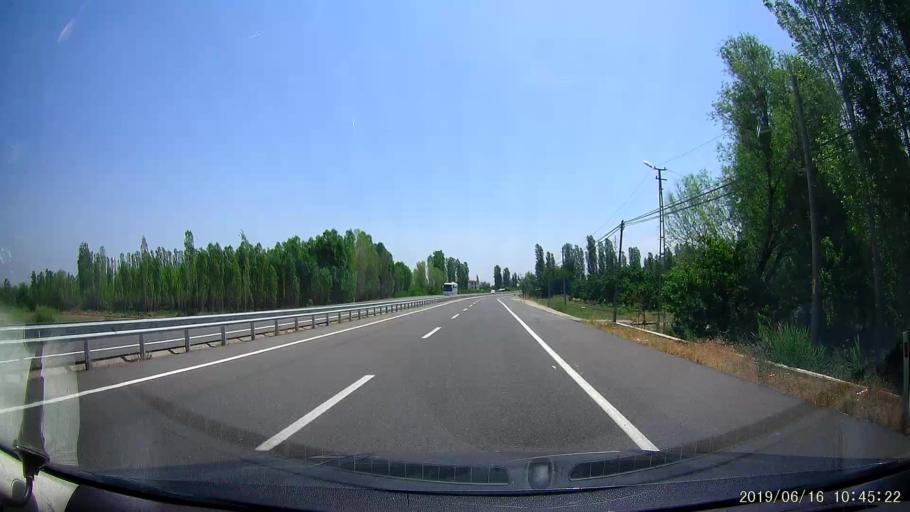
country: AM
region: Armavir
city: Shenavan
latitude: 40.0276
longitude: 43.8684
